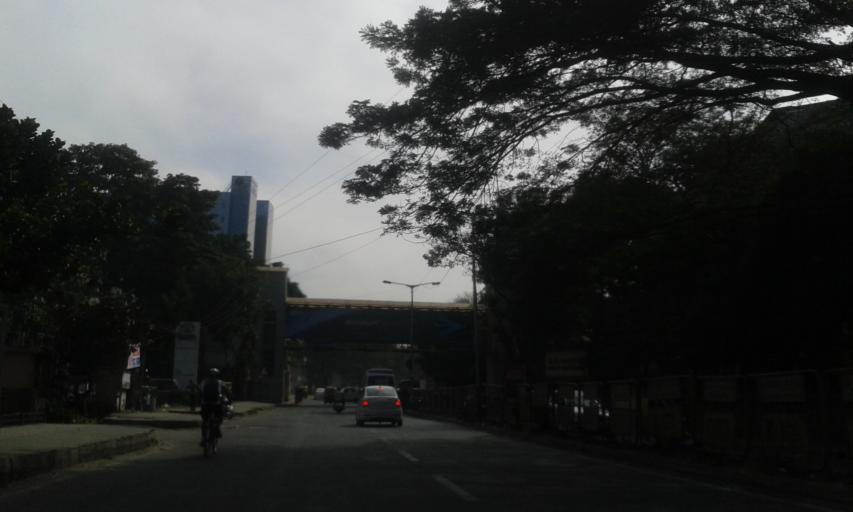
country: IN
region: Karnataka
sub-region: Bangalore Urban
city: Bangalore
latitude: 12.9367
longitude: 77.6054
